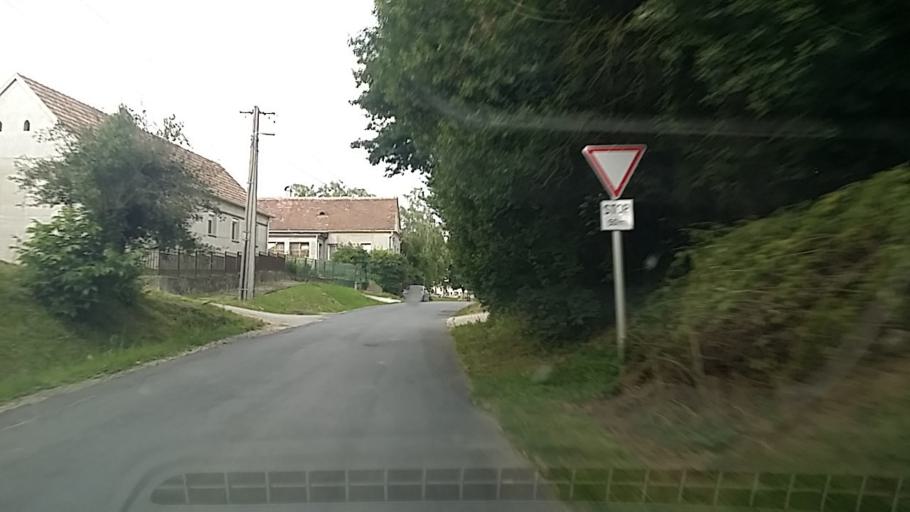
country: HU
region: Zala
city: Nagykanizsa
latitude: 46.4936
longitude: 17.0514
